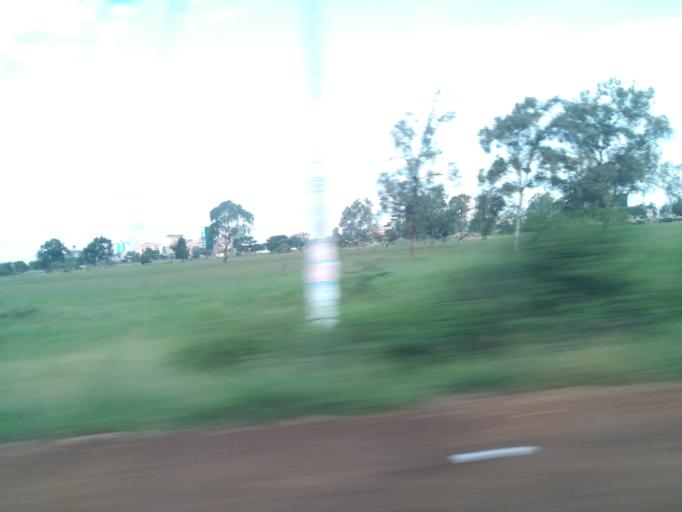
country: KE
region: Nairobi Area
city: Thika
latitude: -1.0408
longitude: 37.0591
